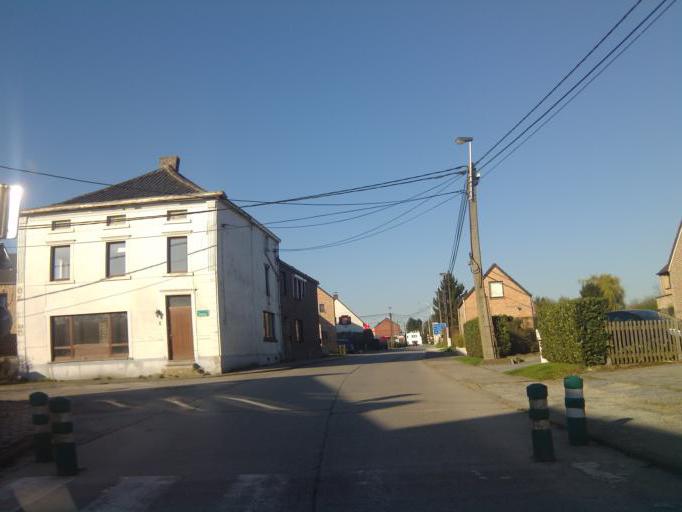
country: BE
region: Wallonia
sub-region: Province du Brabant Wallon
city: Chastre-Villeroux-Blanmont
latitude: 50.6458
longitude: 4.6492
